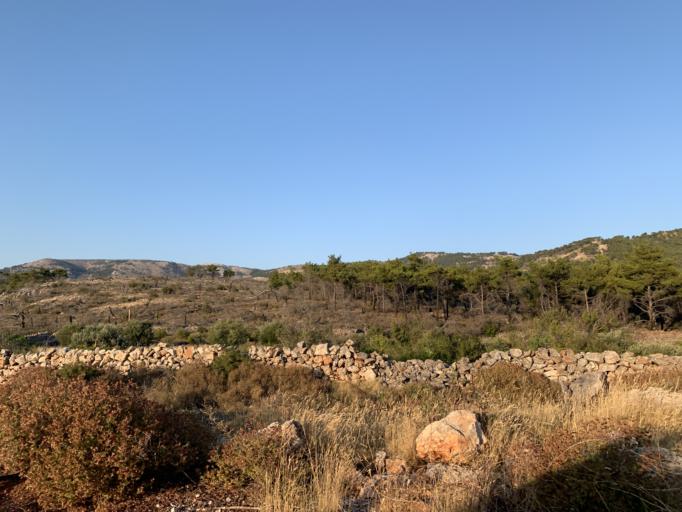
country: GR
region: North Aegean
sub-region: Chios
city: Vrontados
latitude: 38.3821
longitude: 26.0181
